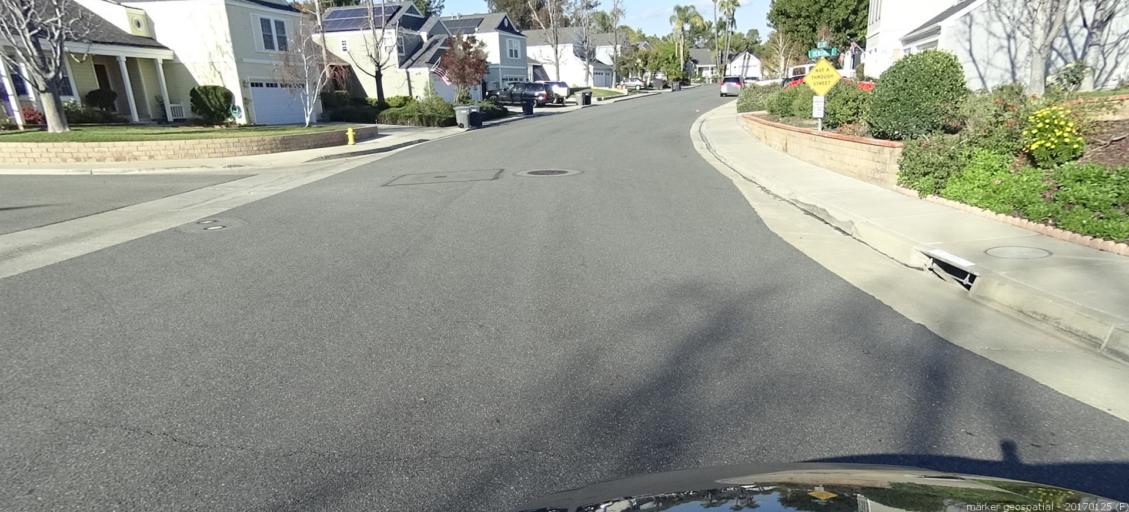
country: US
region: California
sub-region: Orange County
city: Lake Forest
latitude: 33.6459
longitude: -117.6761
